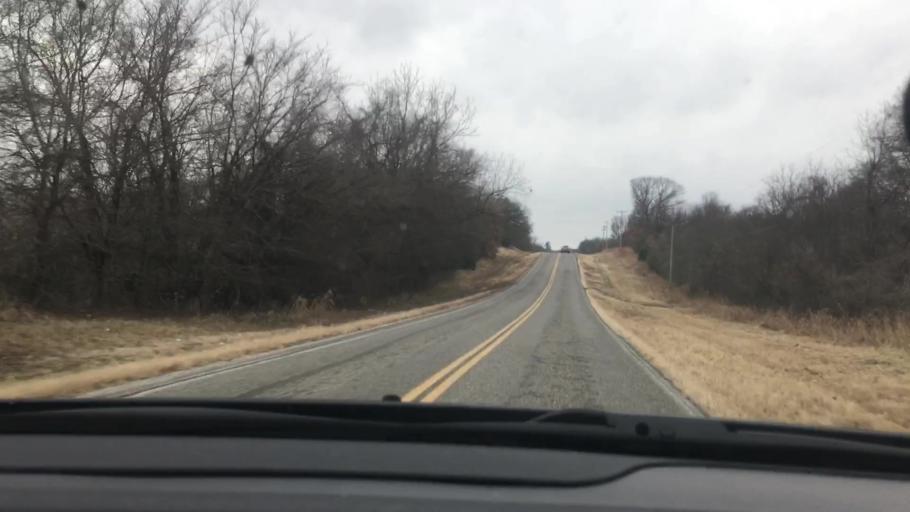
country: US
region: Oklahoma
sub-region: Johnston County
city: Tishomingo
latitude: 34.2220
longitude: -96.6361
